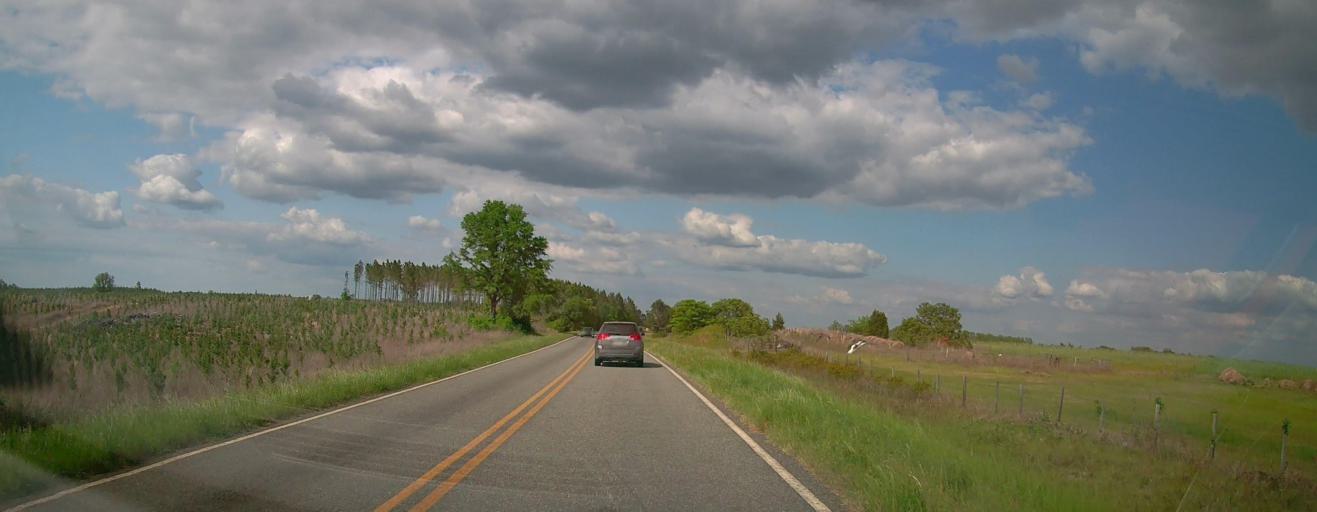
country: US
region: Georgia
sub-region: Laurens County
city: East Dublin
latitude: 32.7233
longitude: -82.9136
